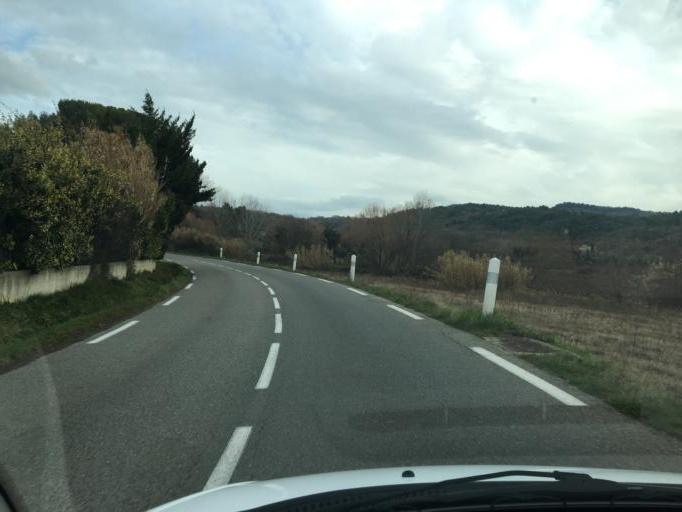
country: FR
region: Provence-Alpes-Cote d'Azur
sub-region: Departement du Vaucluse
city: Mazan
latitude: 44.0514
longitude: 5.1539
